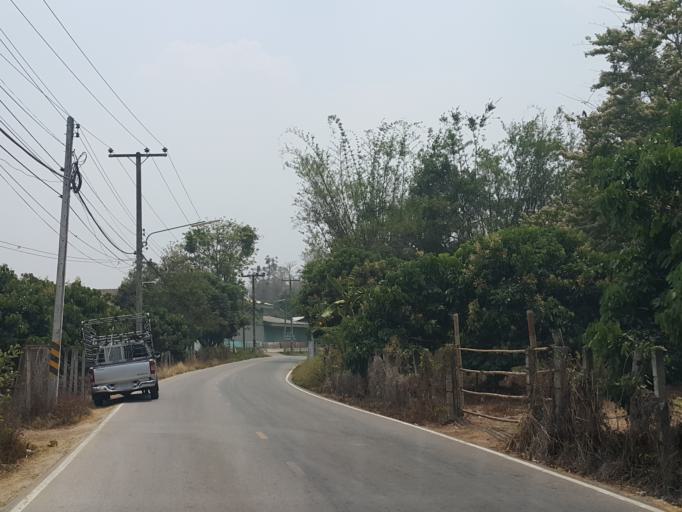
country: TH
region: Chiang Mai
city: Mae Taeng
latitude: 19.0414
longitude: 98.8694
